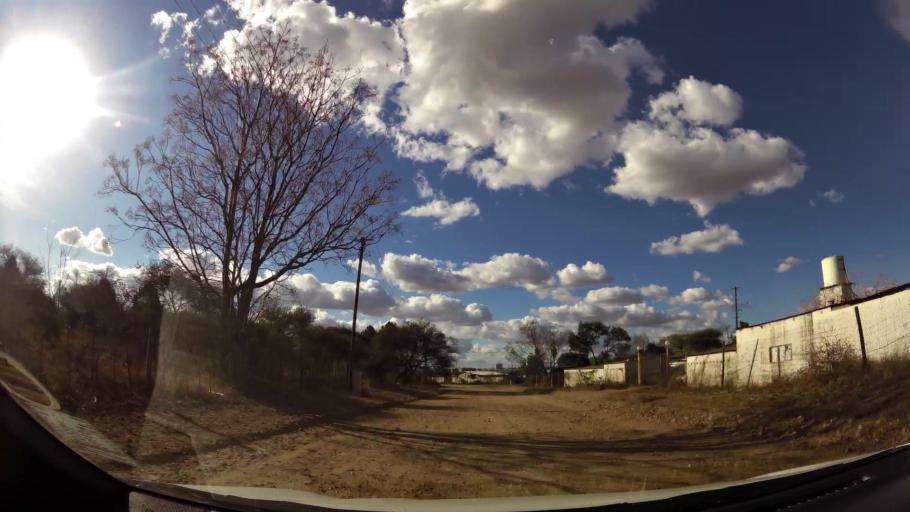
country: ZA
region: Limpopo
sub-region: Capricorn District Municipality
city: Polokwane
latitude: -23.9308
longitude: 29.4454
